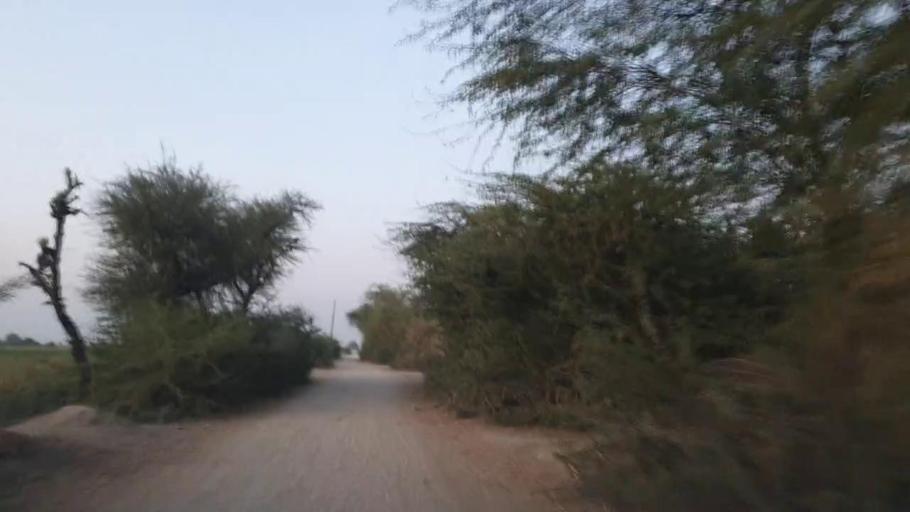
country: PK
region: Sindh
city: Naukot
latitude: 24.9969
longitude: 69.4246
